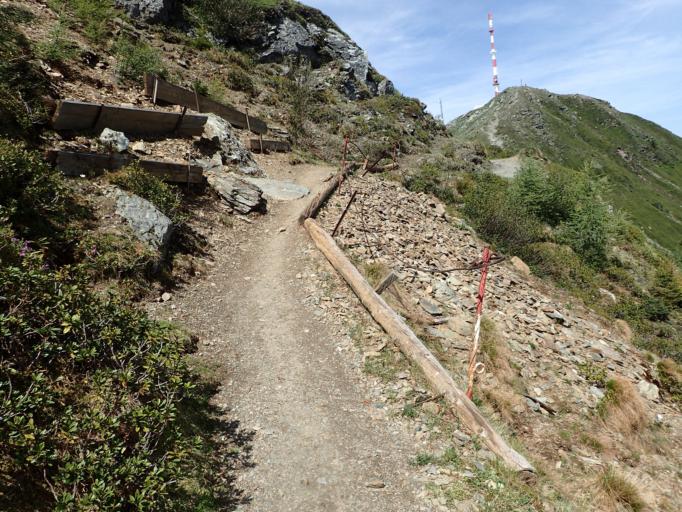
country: AT
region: Carinthia
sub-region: Politischer Bezirk Spittal an der Drau
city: Baldramsdorf
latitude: 46.7572
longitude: 13.4628
